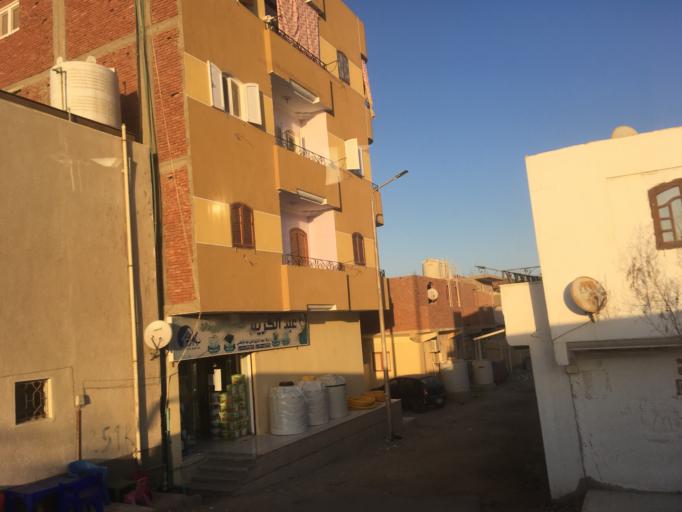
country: EG
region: Red Sea
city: Al Qusayr
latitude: 26.1130
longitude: 34.2774
